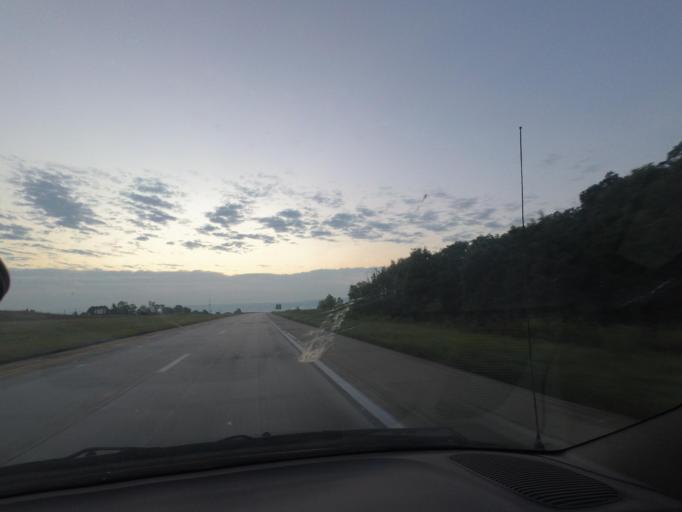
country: US
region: Missouri
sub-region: Macon County
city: Macon
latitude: 39.7585
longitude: -92.6466
